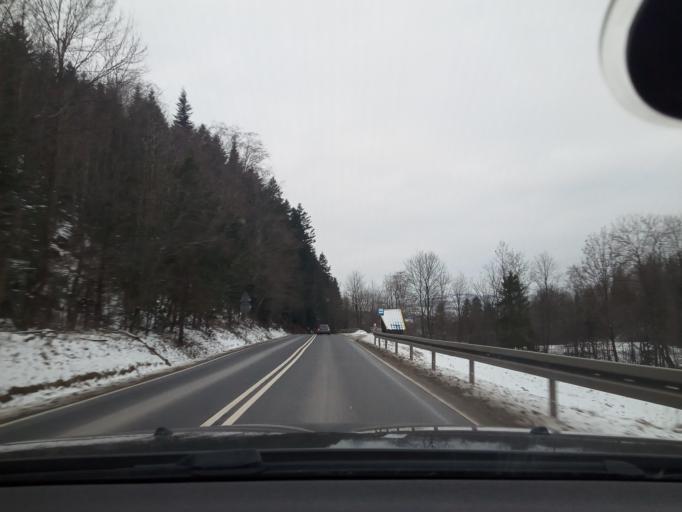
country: PL
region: Lesser Poland Voivodeship
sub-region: Powiat limanowski
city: Lubomierz
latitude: 49.6185
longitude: 20.1624
